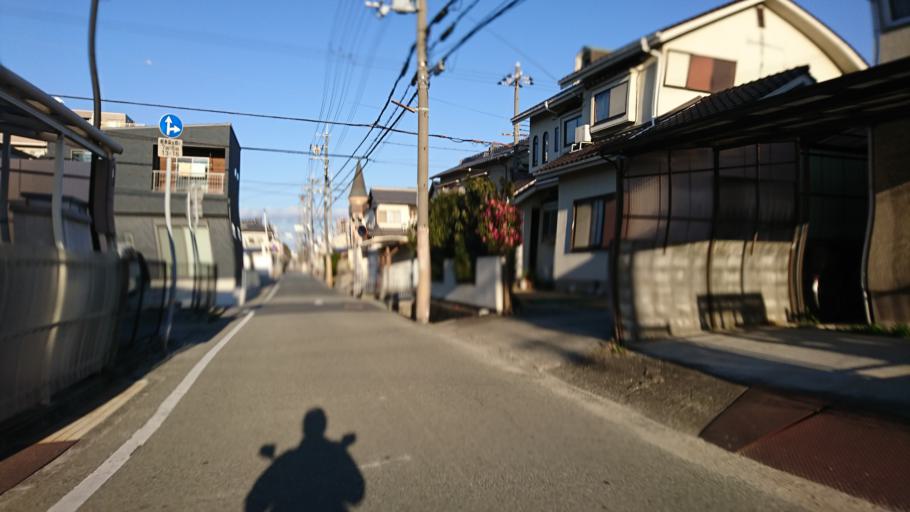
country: JP
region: Hyogo
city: Kakogawacho-honmachi
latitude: 34.7660
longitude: 134.8259
